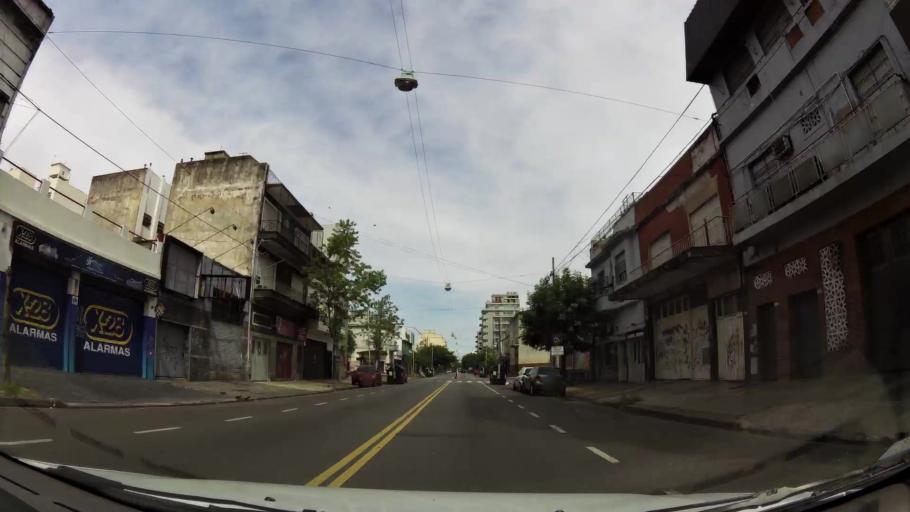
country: AR
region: Buenos Aires F.D.
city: Villa Santa Rita
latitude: -34.6215
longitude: -58.5152
